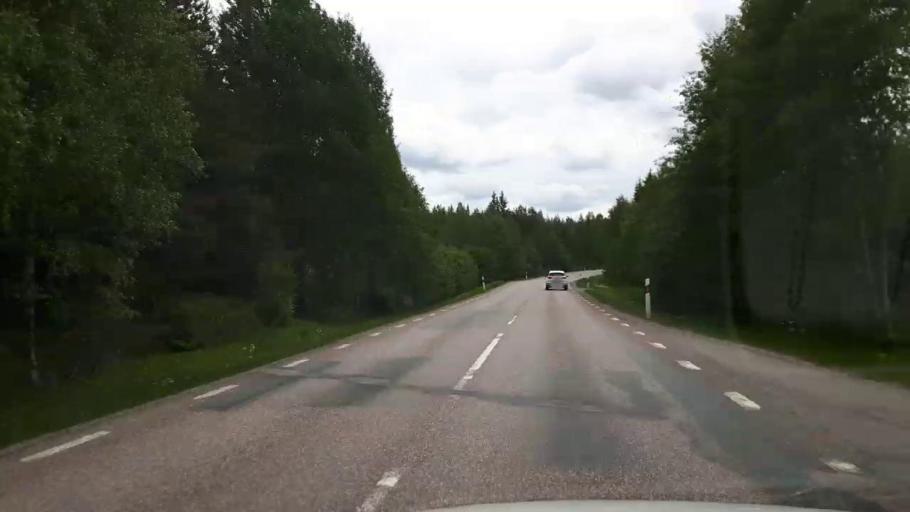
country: SE
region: Vaestmanland
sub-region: Norbergs Kommun
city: Norberg
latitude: 60.1231
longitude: 15.9194
